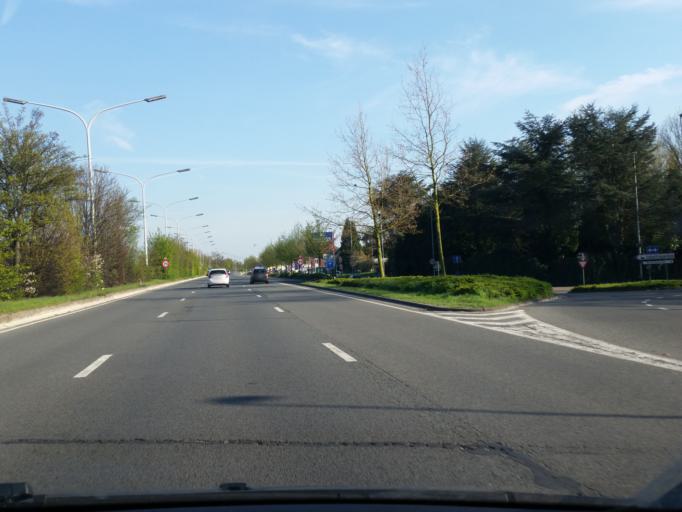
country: BE
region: Flanders
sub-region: Provincie Oost-Vlaanderen
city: Sint-Niklaas
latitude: 51.1525
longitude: 4.1581
